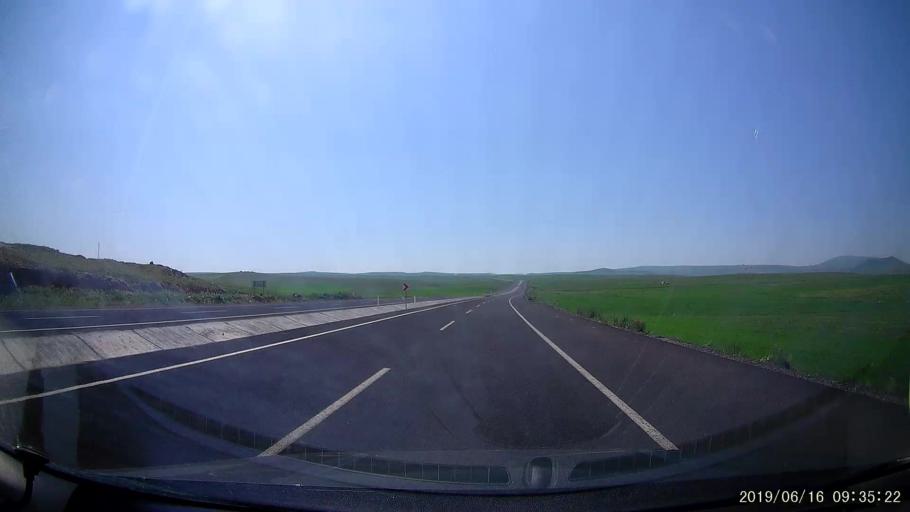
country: TR
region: Kars
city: Kars
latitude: 40.5731
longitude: 43.1547
